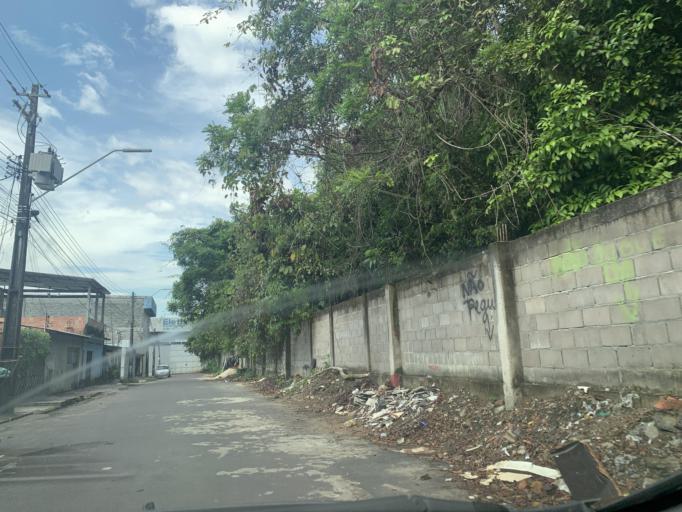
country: BR
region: Amazonas
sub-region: Manaus
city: Manaus
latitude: -3.0943
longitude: -59.9534
